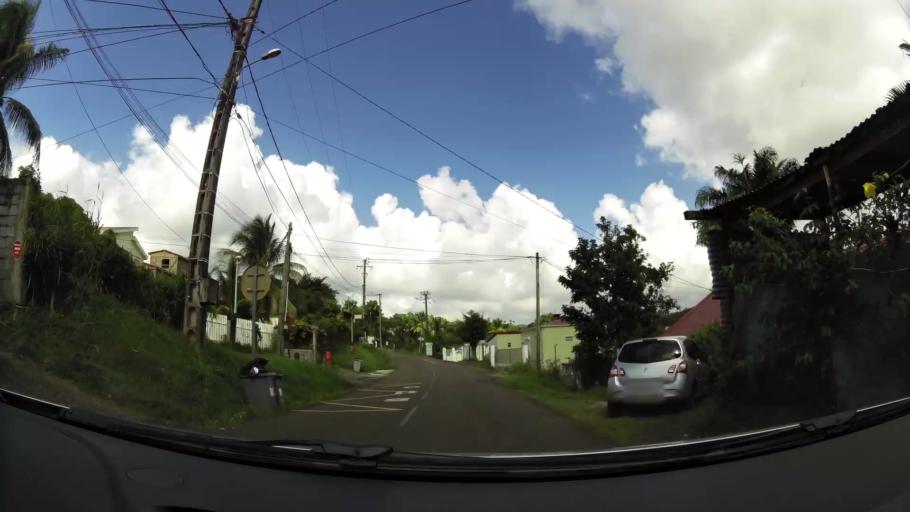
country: MQ
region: Martinique
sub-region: Martinique
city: Fort-de-France
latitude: 14.6317
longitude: -61.0475
